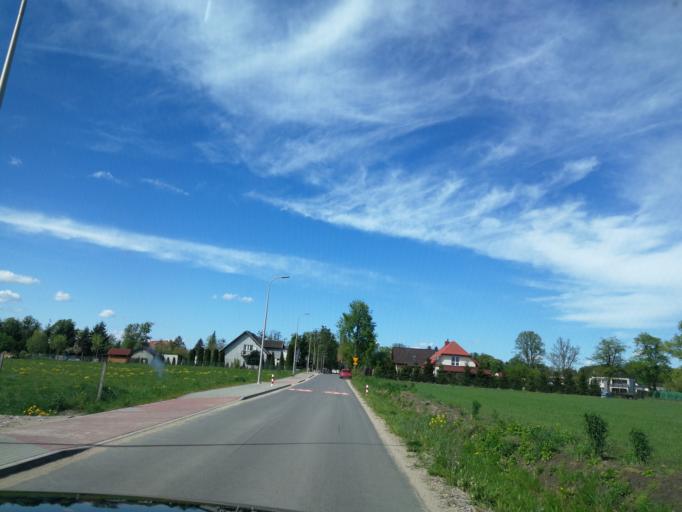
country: PL
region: Warmian-Masurian Voivodeship
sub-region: Powiat ilawski
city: Ilawa
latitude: 53.6274
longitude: 19.6656
